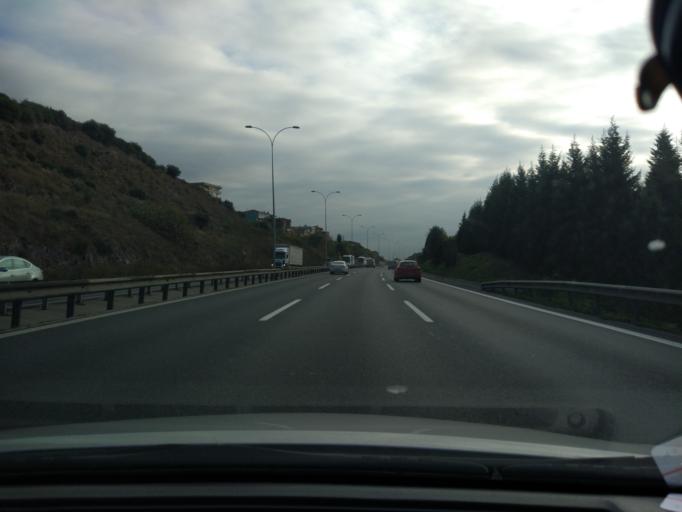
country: TR
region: Kocaeli
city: Korfez
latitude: 40.7789
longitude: 29.7162
